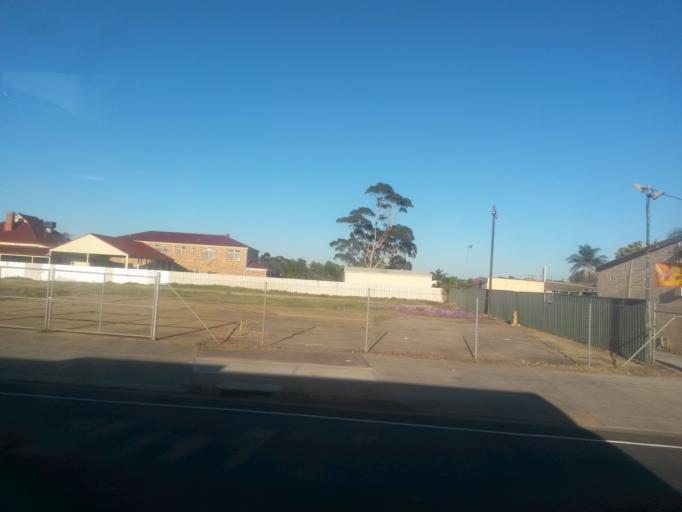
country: AU
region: South Australia
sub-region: Port Adelaide Enfield
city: Alberton
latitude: -34.8573
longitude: 138.5292
